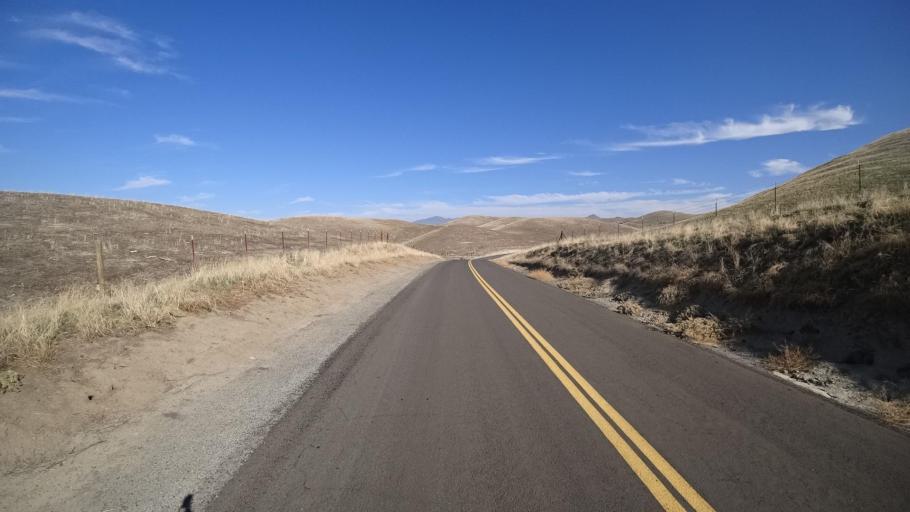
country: US
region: California
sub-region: Tulare County
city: Richgrove
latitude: 35.6709
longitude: -118.9121
